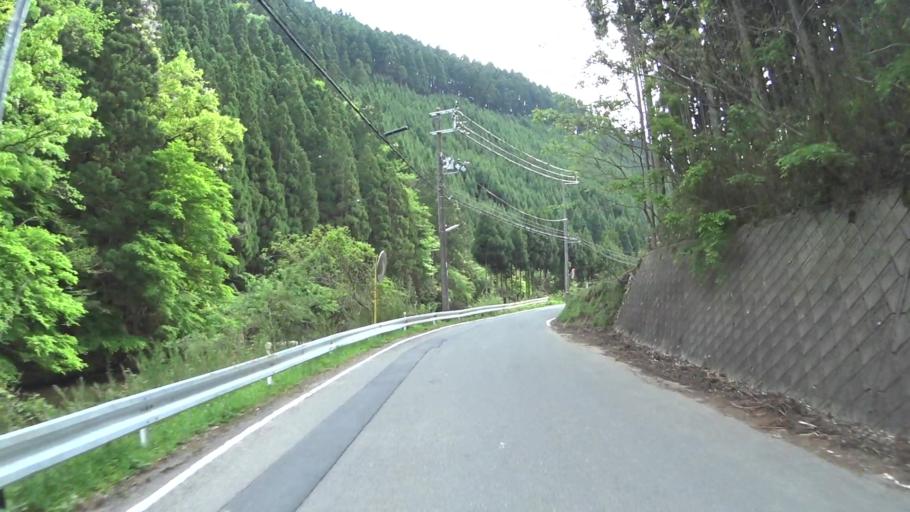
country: JP
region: Kyoto
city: Kameoka
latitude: 35.1204
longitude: 135.6150
